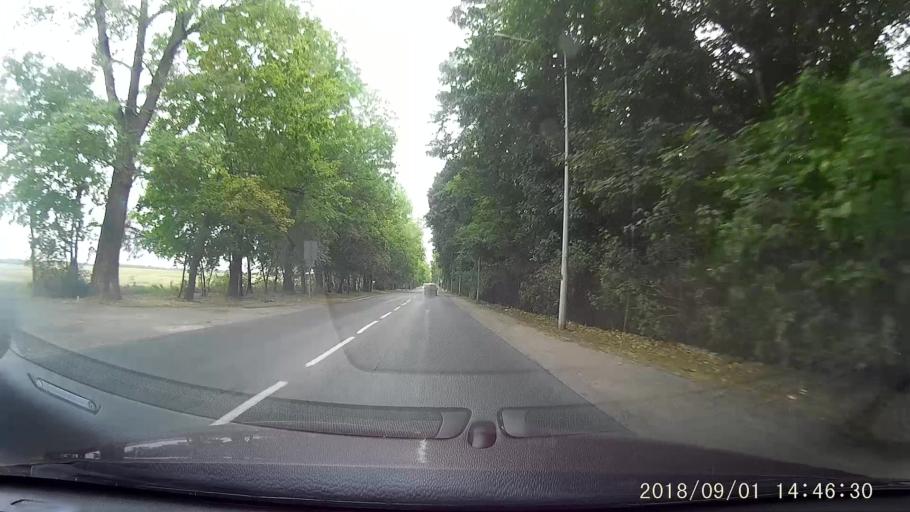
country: PL
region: Lubusz
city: Gorzow Wielkopolski
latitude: 52.7419
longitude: 15.1744
